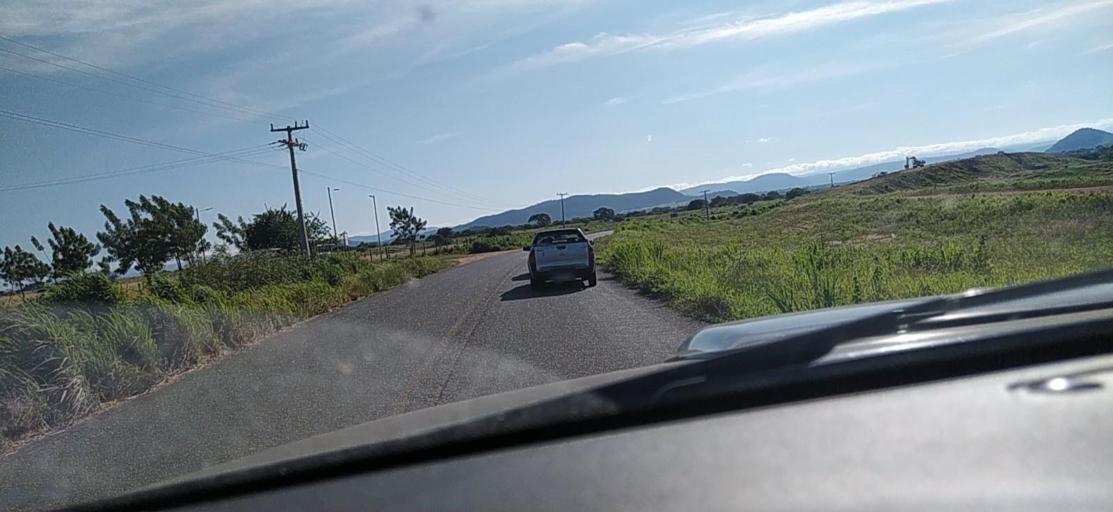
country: BR
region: Bahia
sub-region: Guanambi
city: Guanambi
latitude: -14.1473
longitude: -42.8338
